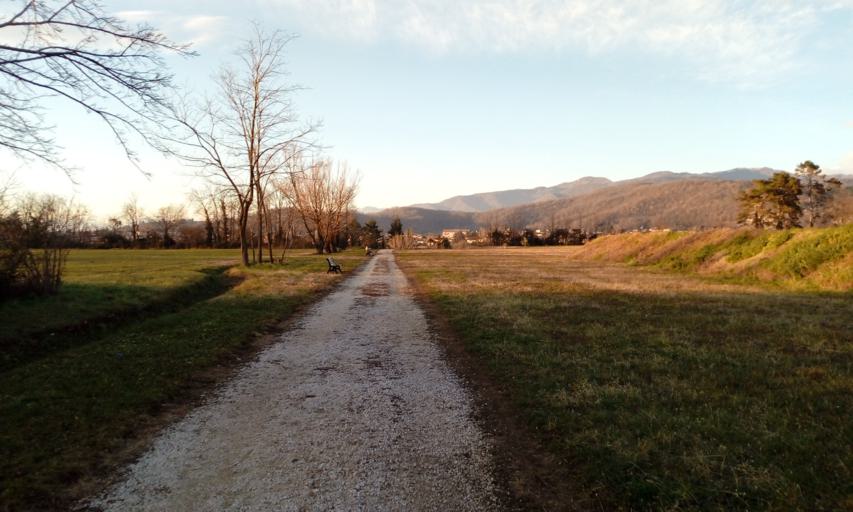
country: IT
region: Friuli Venezia Giulia
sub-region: Provincia di Udine
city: Cividale del Friuli
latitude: 46.0923
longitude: 13.4431
